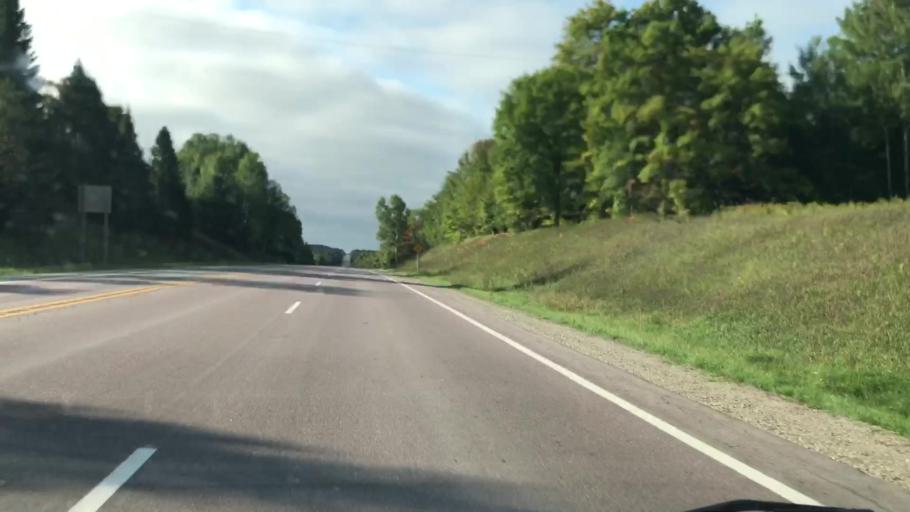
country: US
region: Michigan
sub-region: Luce County
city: Newberry
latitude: 46.3068
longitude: -85.5676
